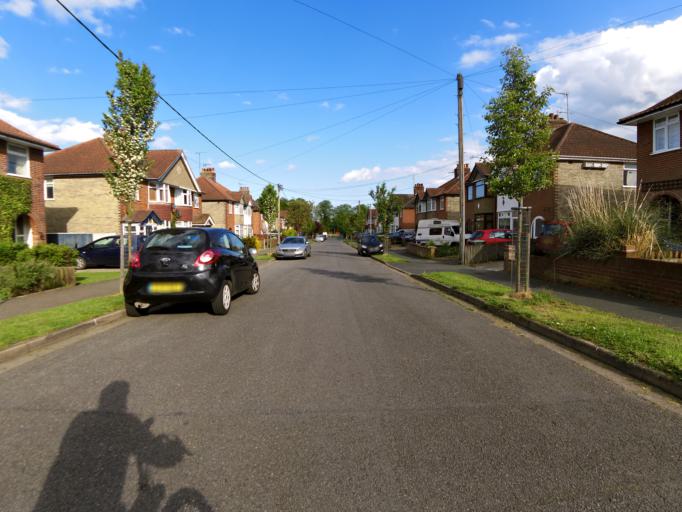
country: GB
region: England
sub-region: Suffolk
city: Stowmarket
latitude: 52.1901
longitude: 0.9847
